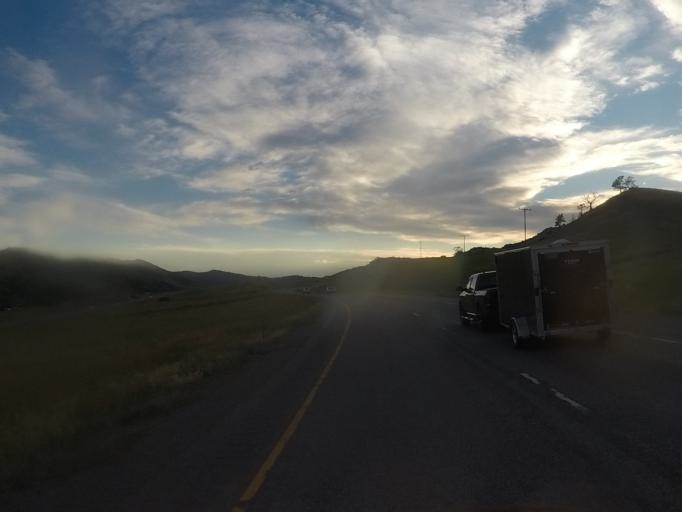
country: US
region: Montana
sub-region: Park County
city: Livingston
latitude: 45.6645
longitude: -110.6850
